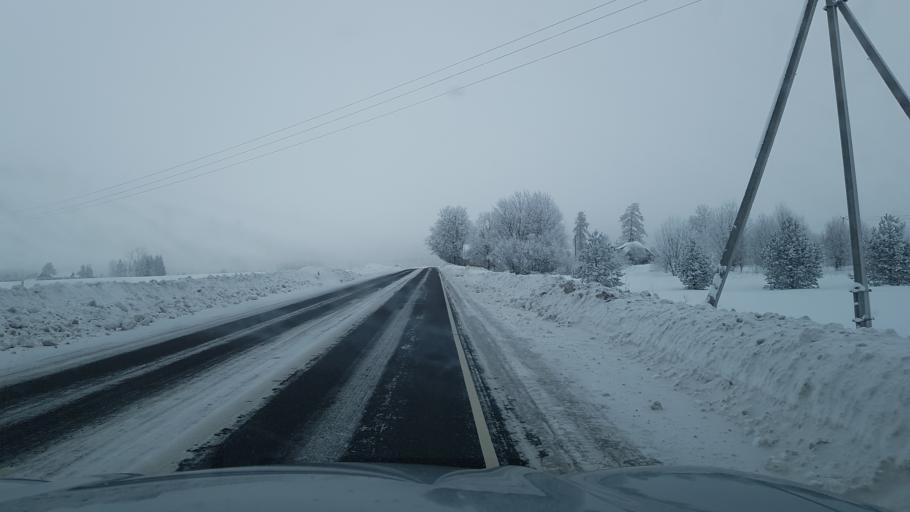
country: EE
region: Ida-Virumaa
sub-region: Johvi vald
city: Johvi
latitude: 59.2611
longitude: 27.3839
